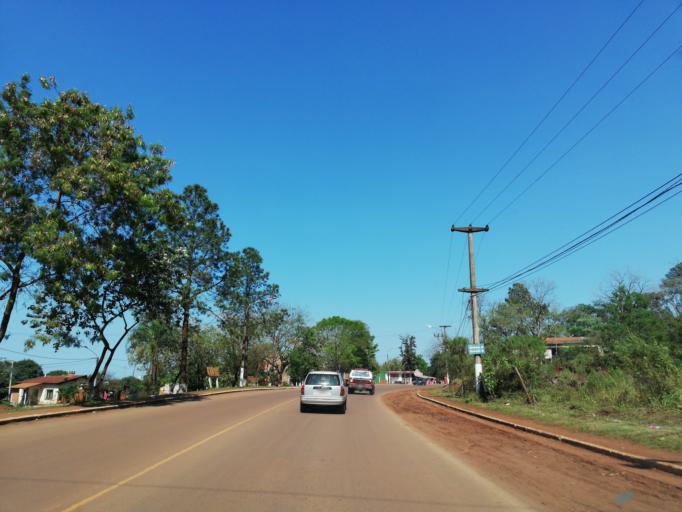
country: AR
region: Misiones
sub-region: Departamento de Eldorado
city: Eldorado
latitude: -26.4068
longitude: -54.6510
